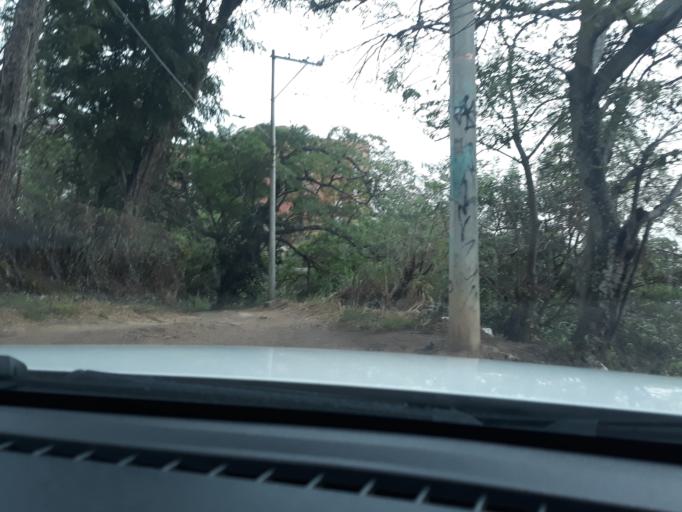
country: CO
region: Valle del Cauca
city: Cali
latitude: 3.4316
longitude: -76.5498
